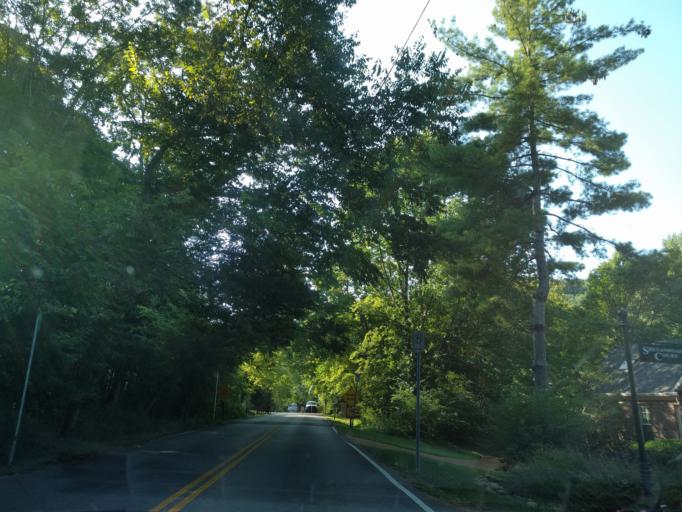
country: US
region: Tennessee
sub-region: Davidson County
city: Forest Hills
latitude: 36.0641
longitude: -86.8109
